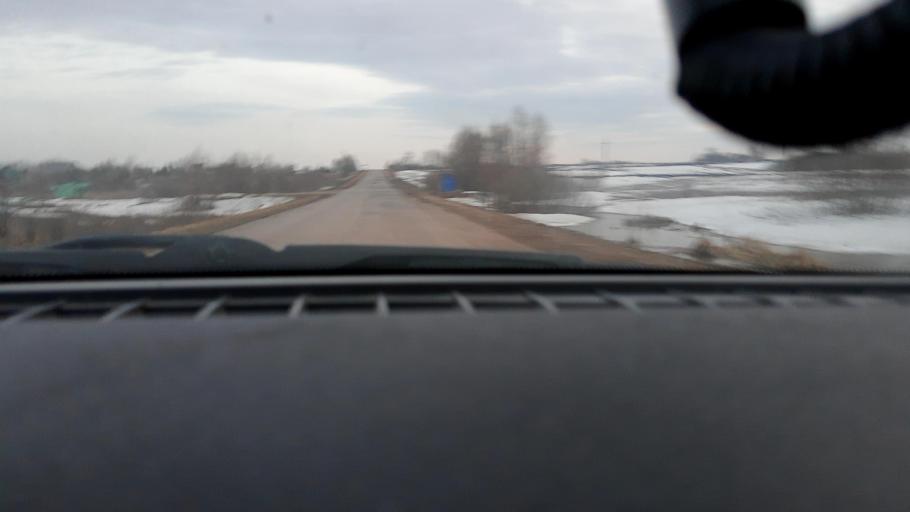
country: RU
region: Bashkortostan
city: Iglino
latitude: 54.6349
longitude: 56.4246
